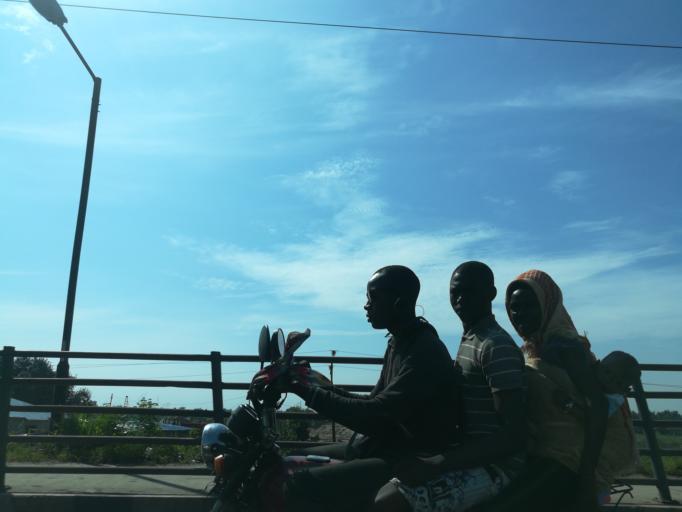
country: NG
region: Lagos
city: Ebute Ikorodu
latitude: 6.6097
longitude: 3.4401
